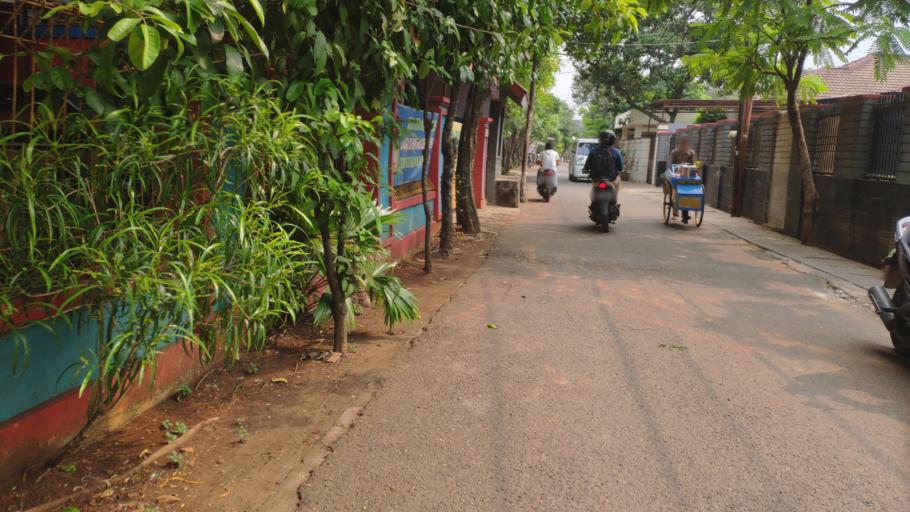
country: ID
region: West Java
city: Depok
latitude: -6.3493
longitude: 106.8111
